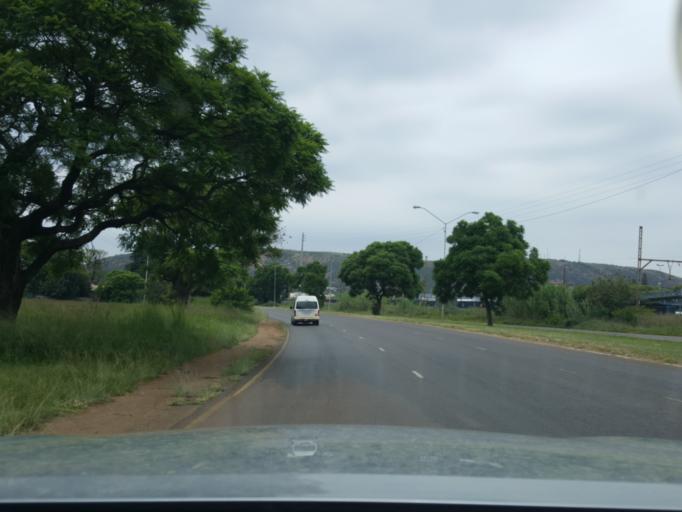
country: ZA
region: Gauteng
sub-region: City of Tshwane Metropolitan Municipality
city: Pretoria
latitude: -25.6698
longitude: 28.1830
